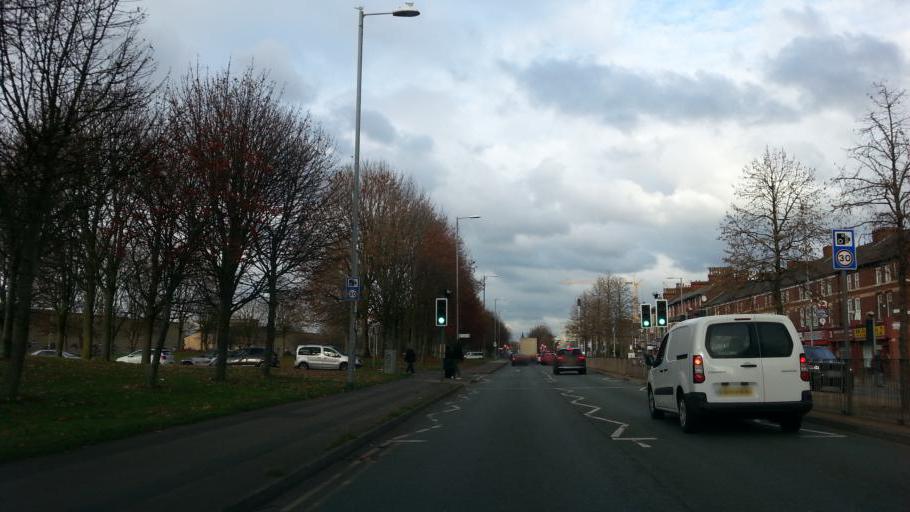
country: GB
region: England
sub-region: Manchester
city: Hulme
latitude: 53.4547
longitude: -2.2453
